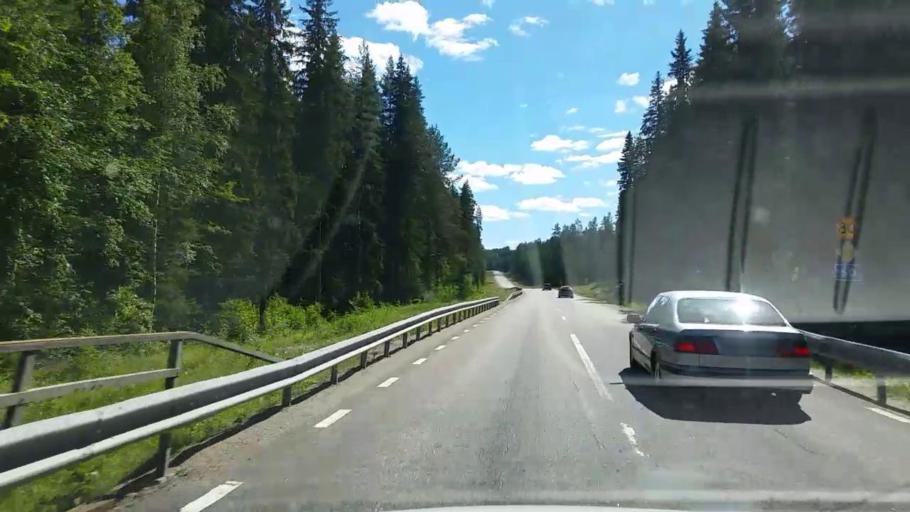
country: SE
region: Gaevleborg
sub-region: Ovanakers Kommun
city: Edsbyn
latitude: 61.1691
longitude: 15.8831
